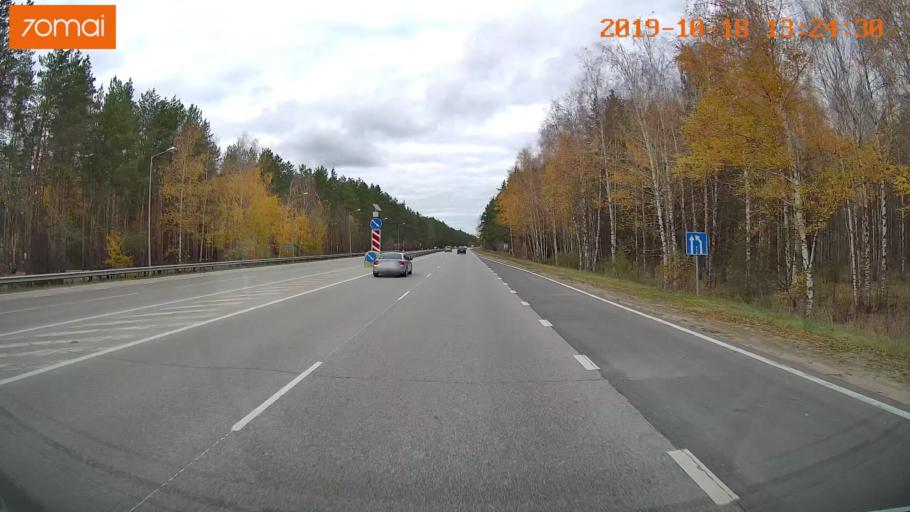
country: RU
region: Rjazan
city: Polyany
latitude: 54.7316
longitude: 39.8435
